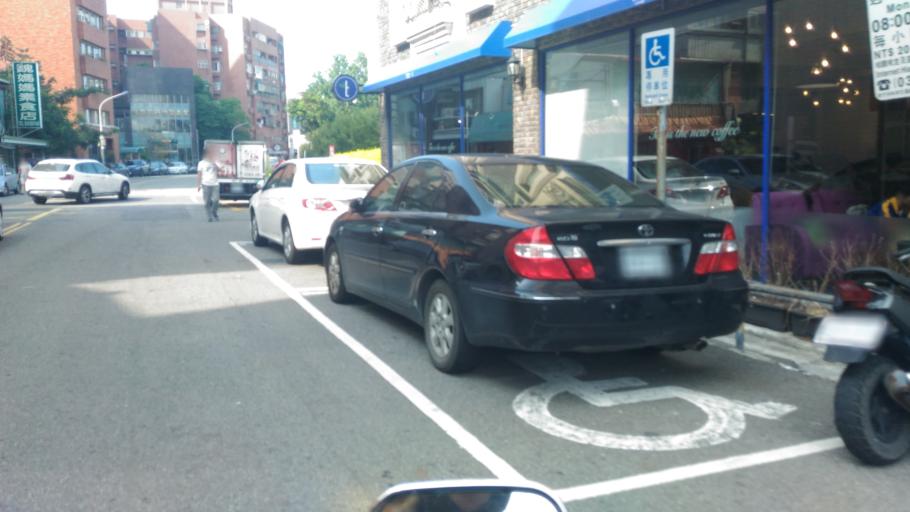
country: TW
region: Taiwan
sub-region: Hsinchu
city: Hsinchu
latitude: 24.8102
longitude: 120.9682
